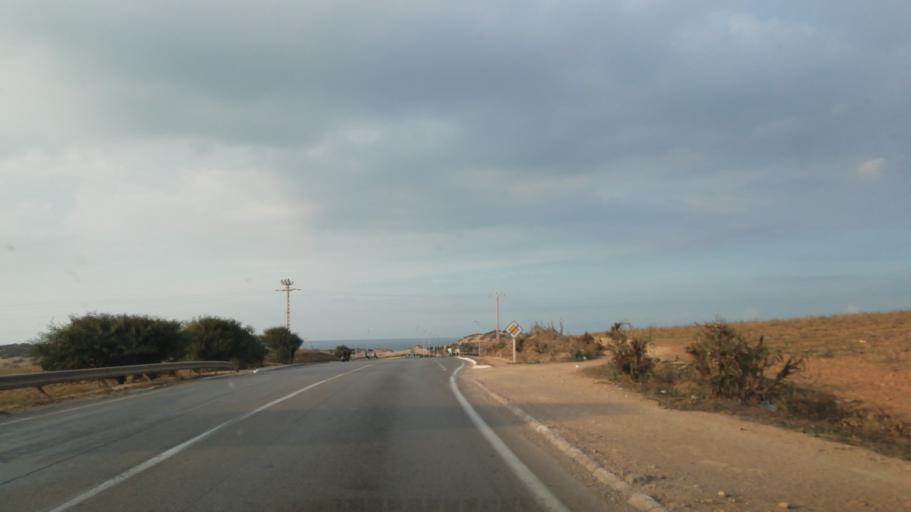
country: DZ
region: Oran
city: Ain el Bya
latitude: 35.7846
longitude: -0.1012
